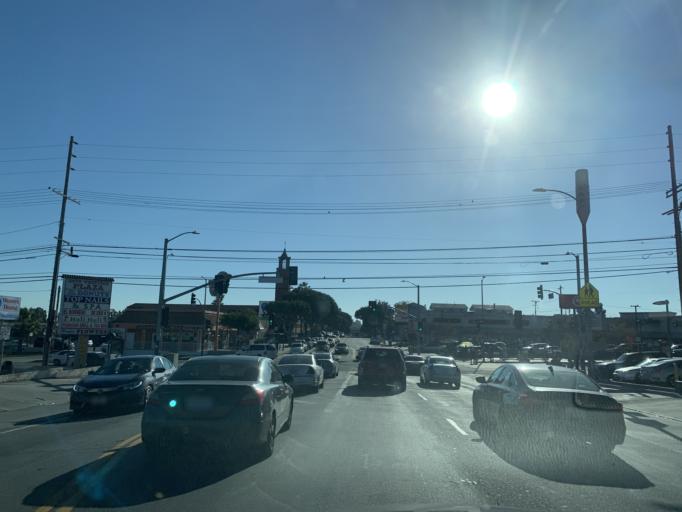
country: US
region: California
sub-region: Los Angeles County
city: Boyle Heights
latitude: 34.0347
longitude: -118.2153
